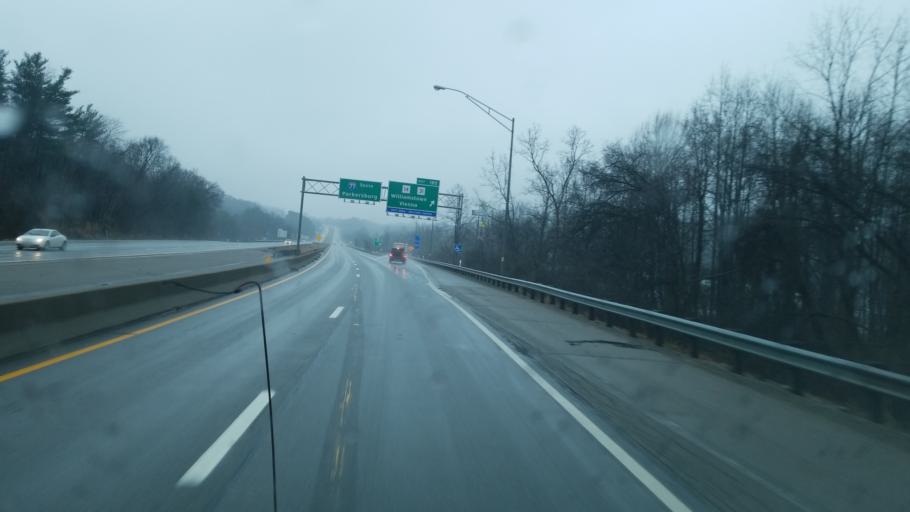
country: US
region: West Virginia
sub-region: Wood County
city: Williamstown
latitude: 39.3929
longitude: -81.4395
